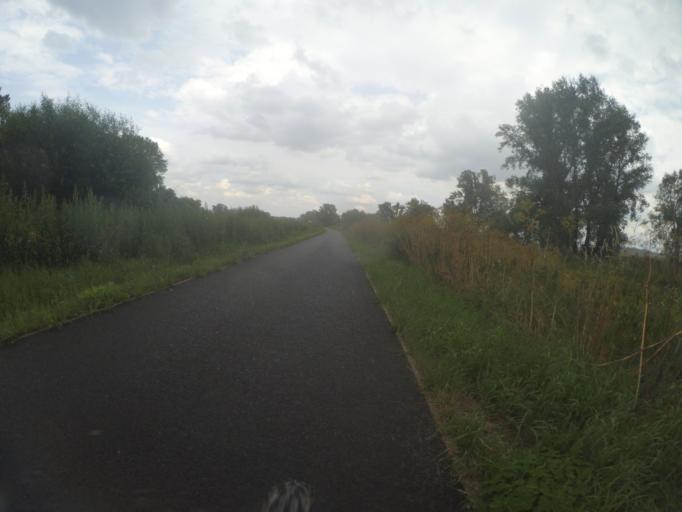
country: CZ
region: Central Bohemia
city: Luzec nad Vltavou
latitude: 50.3191
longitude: 14.4435
